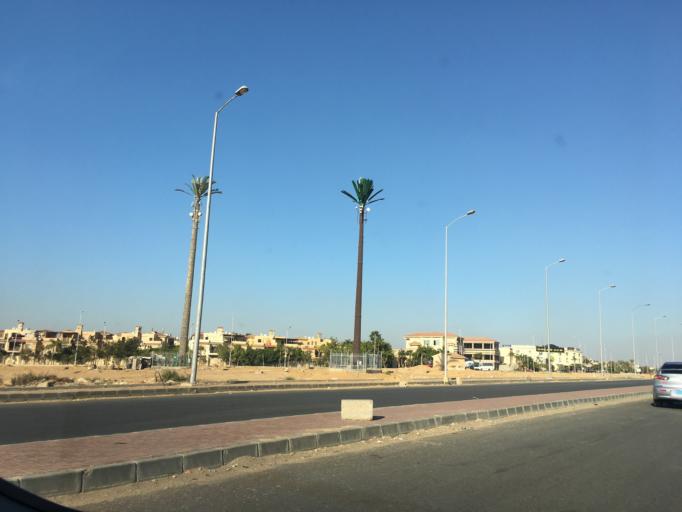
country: EG
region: Al Jizah
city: Madinat Sittah Uktubar
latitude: 29.9987
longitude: 30.9571
